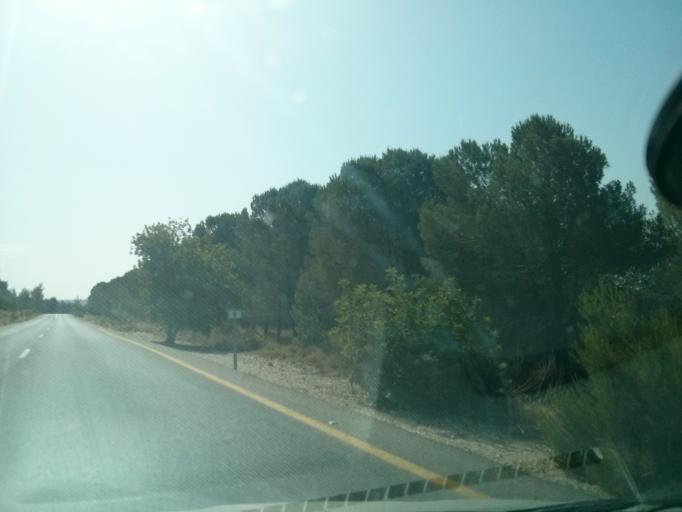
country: PS
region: West Bank
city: Surif
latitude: 31.6750
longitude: 35.0429
